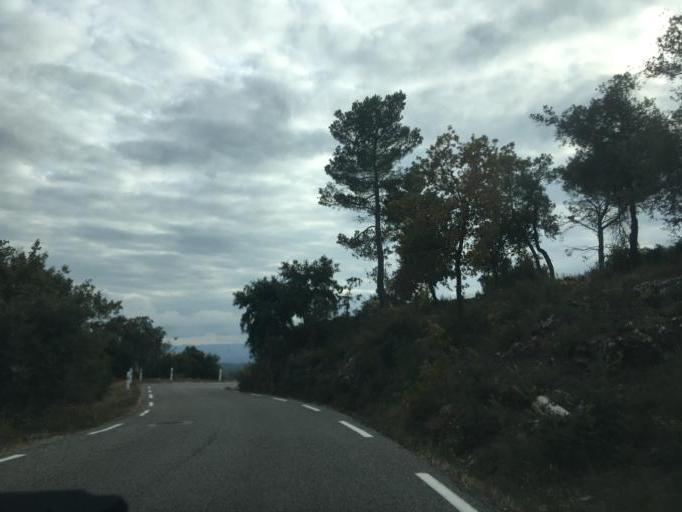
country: FR
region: Provence-Alpes-Cote d'Azur
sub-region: Departement du Var
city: Villecroze
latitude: 43.5853
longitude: 6.3092
